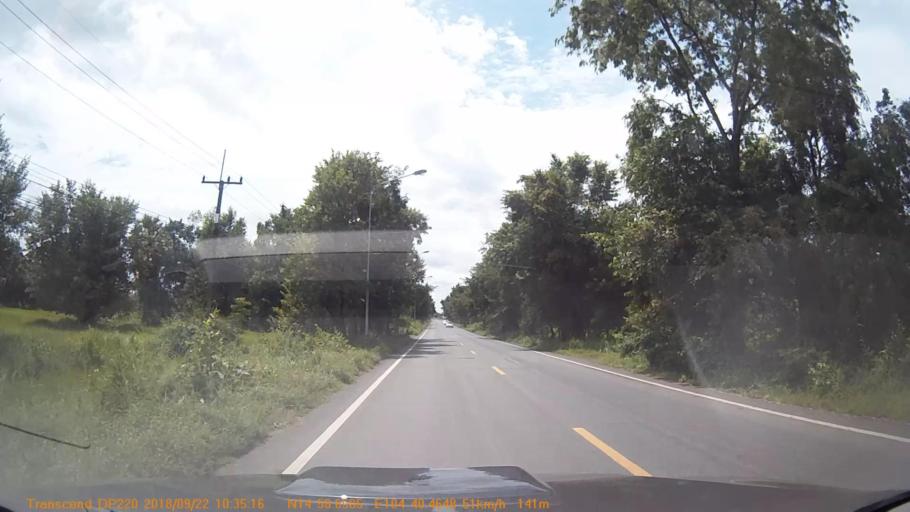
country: TH
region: Sisaket
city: Benchalak
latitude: 14.8442
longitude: 104.6744
